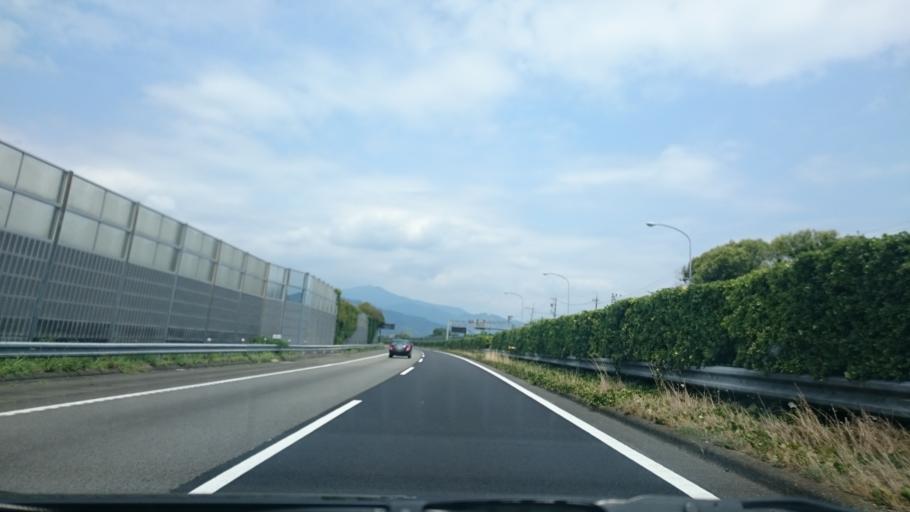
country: JP
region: Shizuoka
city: Shizuoka-shi
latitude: 34.9878
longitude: 138.4356
